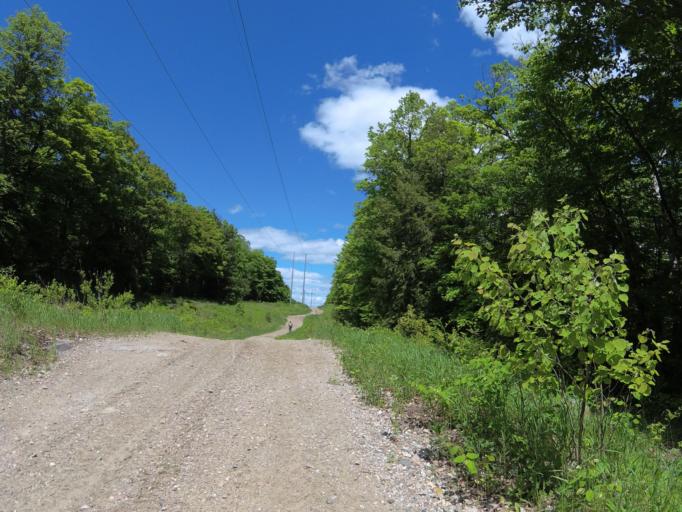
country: CA
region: Ontario
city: Renfrew
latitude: 45.0235
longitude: -76.8874
